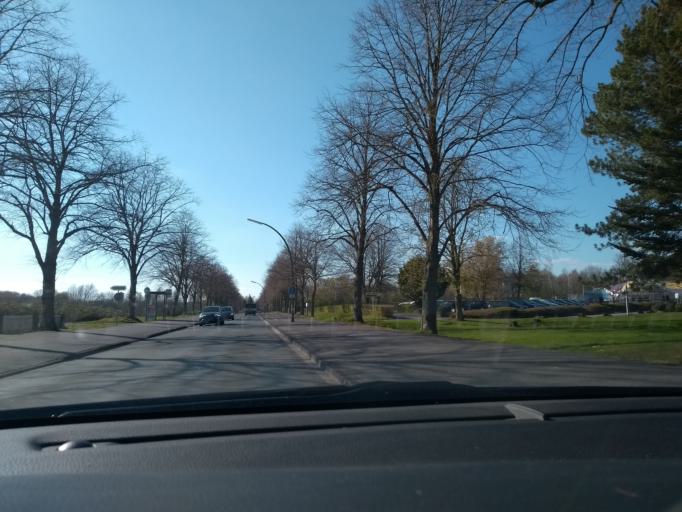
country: DE
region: North Rhine-Westphalia
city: Lunen
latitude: 51.6248
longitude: 7.5022
